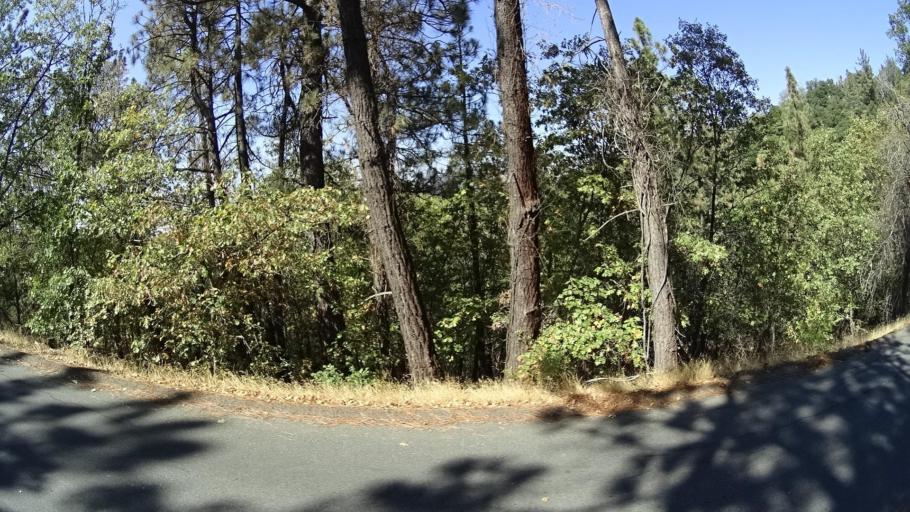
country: US
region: California
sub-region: San Diego County
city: Julian
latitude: 33.0922
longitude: -116.6044
